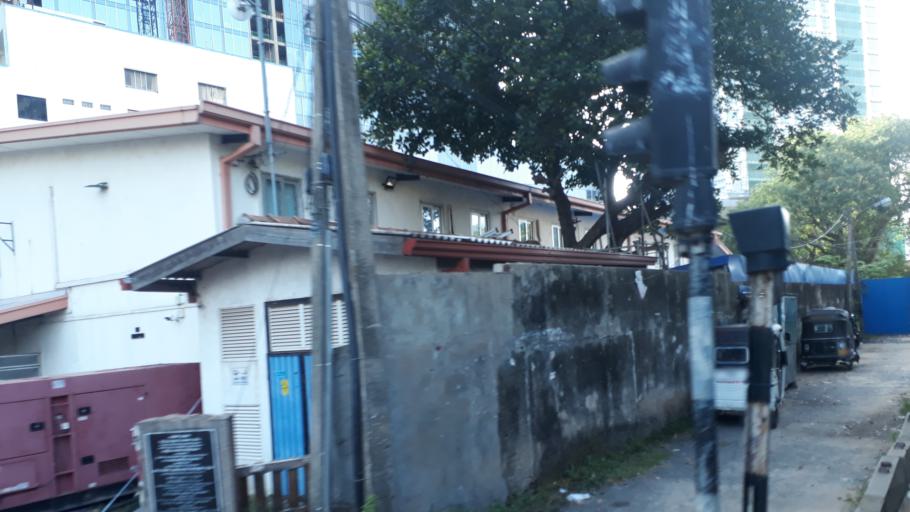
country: LK
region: Western
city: Colombo
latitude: 6.9250
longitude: 79.8491
